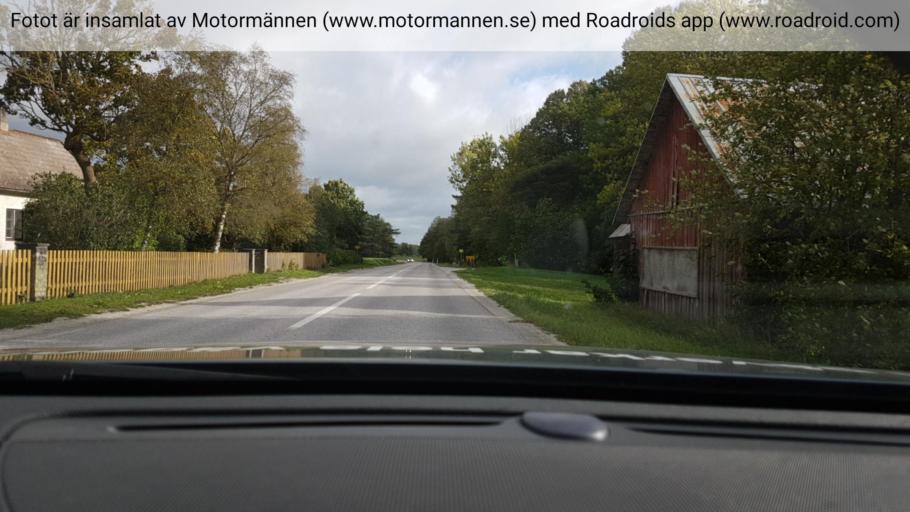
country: SE
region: Gotland
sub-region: Gotland
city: Visby
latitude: 57.6763
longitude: 18.4881
